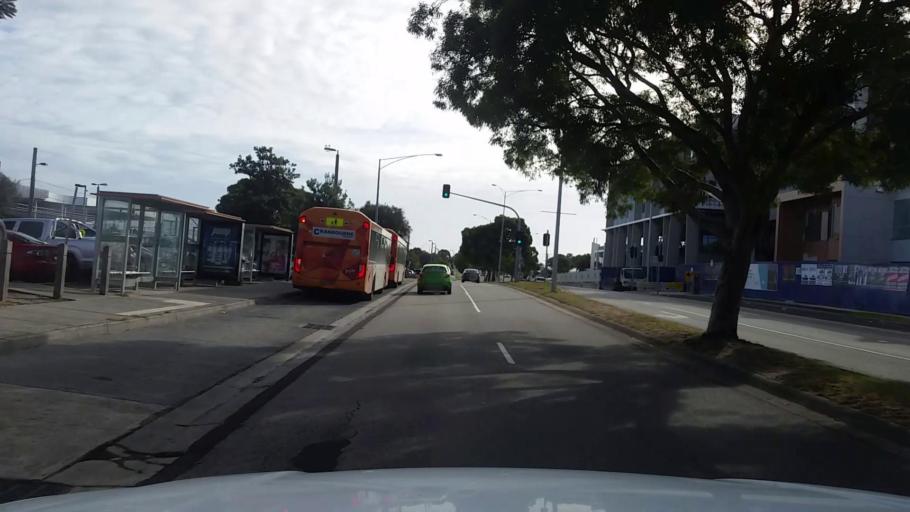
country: AU
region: Victoria
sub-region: Frankston
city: Frankston
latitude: -38.1444
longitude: 145.1262
